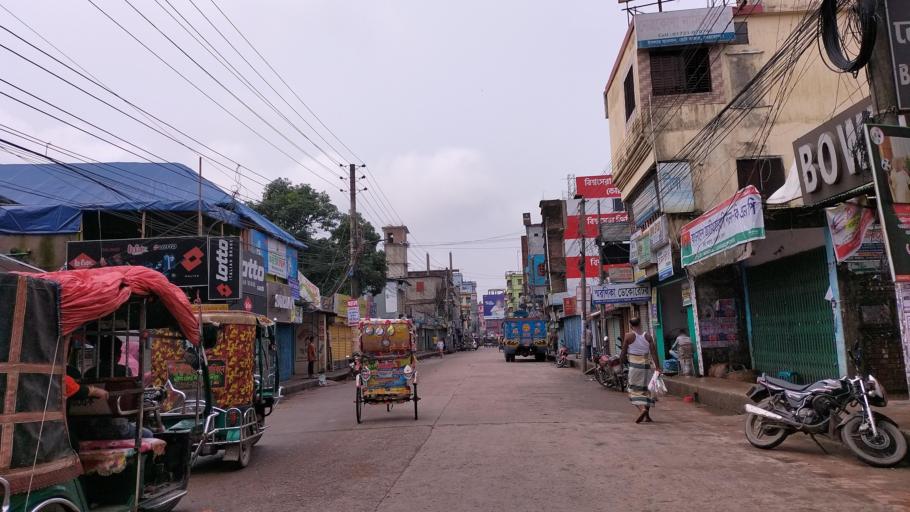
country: BD
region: Dhaka
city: Netrakona
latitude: 24.8817
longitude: 90.7322
